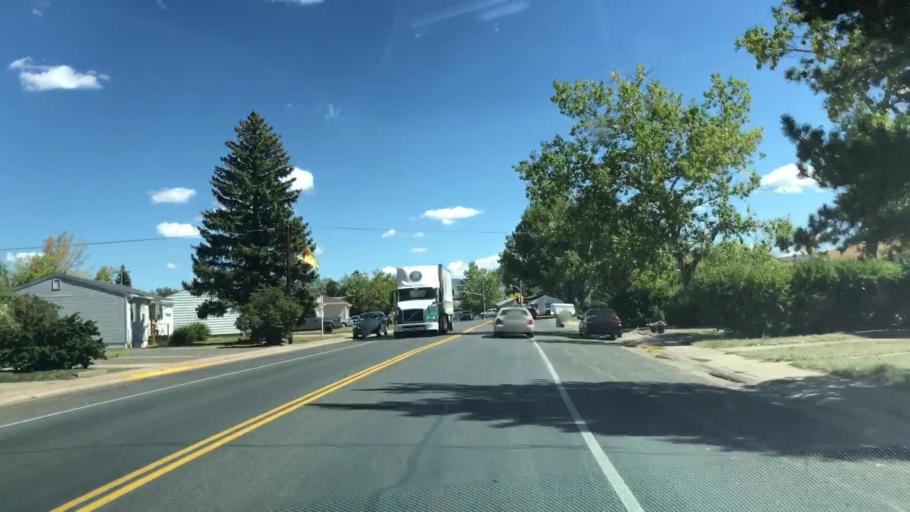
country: US
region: Wyoming
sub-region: Albany County
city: Laramie
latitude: 41.3257
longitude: -105.5860
